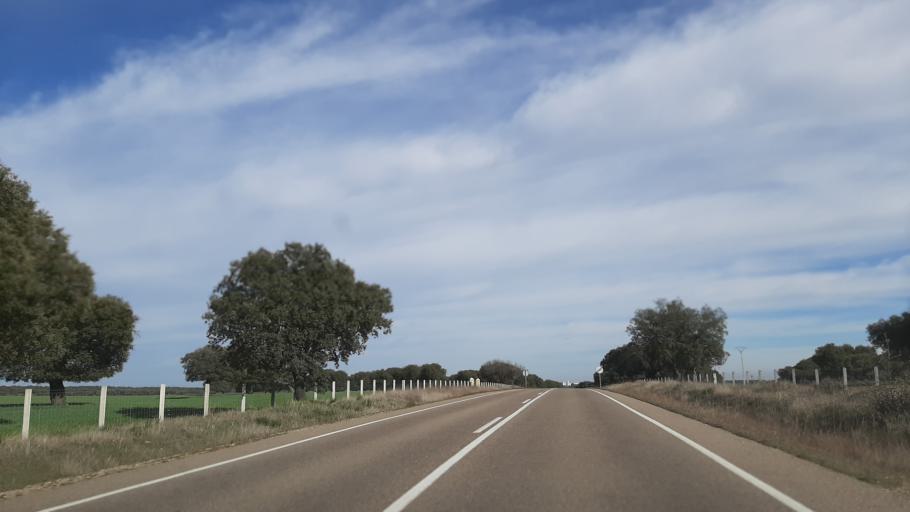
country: ES
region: Castille and Leon
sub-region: Provincia de Salamanca
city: Anover de Tormes
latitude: 41.0894
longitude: -5.9358
